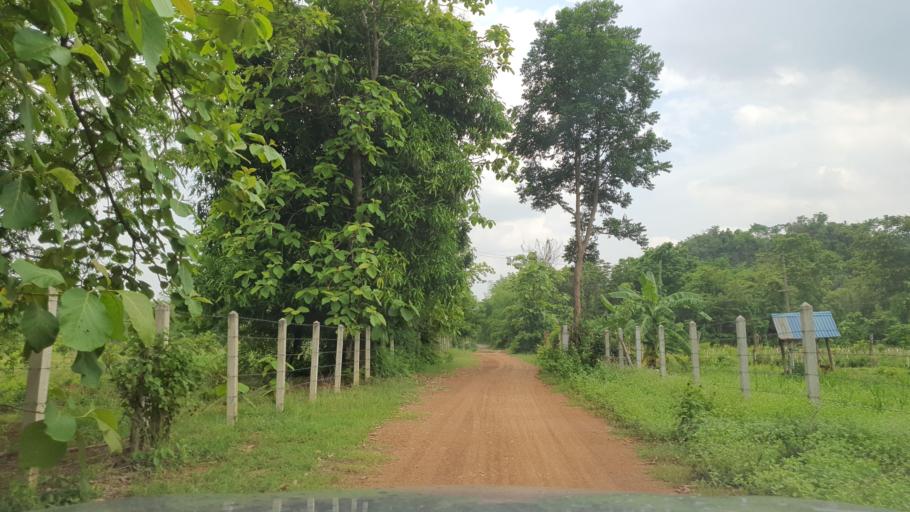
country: TH
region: Sukhothai
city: Thung Saliam
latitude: 17.2459
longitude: 99.5439
